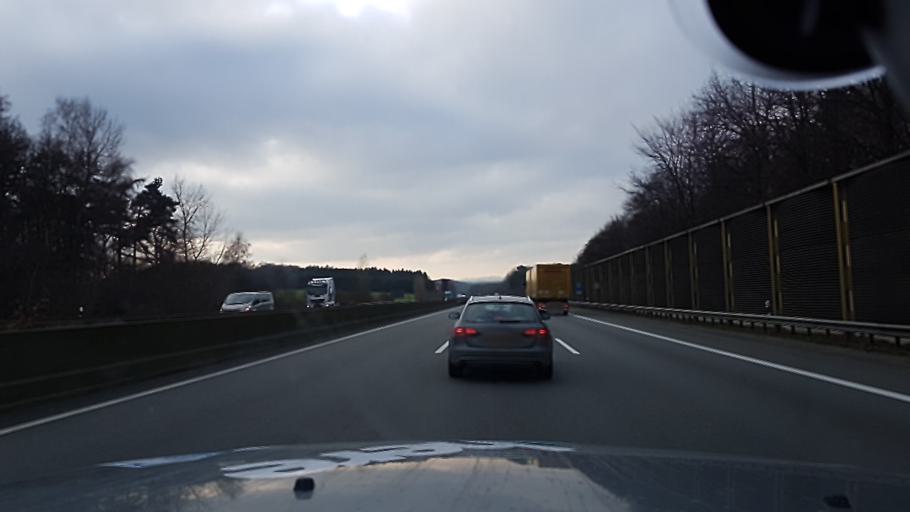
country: DE
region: Lower Saxony
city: Wallenhorst
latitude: 52.3296
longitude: 7.9823
